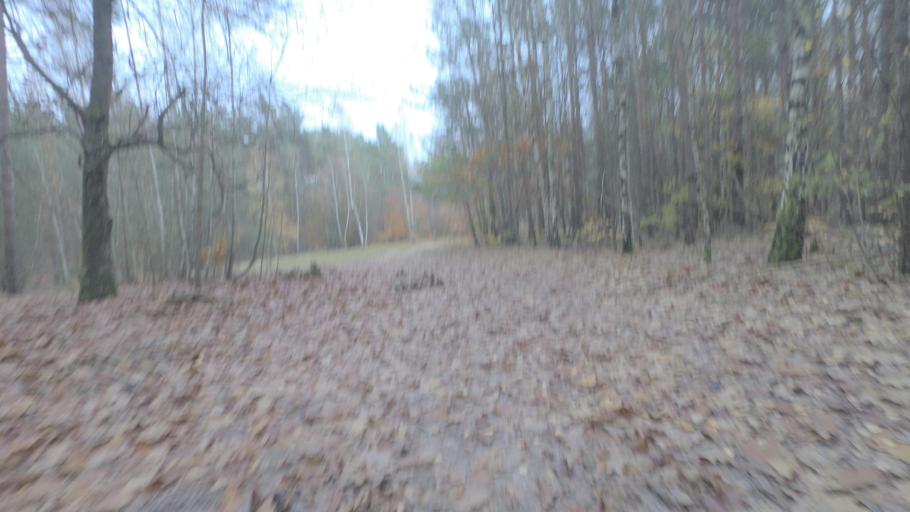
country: DE
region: Brandenburg
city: Rangsdorf
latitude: 52.3197
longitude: 13.4078
